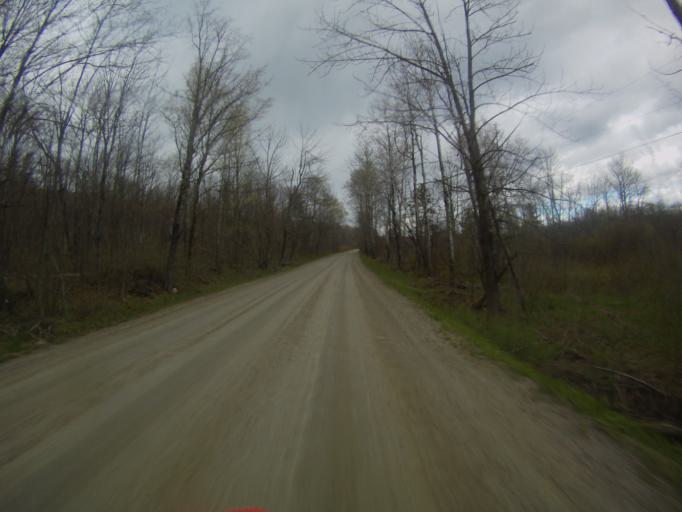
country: US
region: Vermont
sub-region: Addison County
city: Bristol
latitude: 44.0597
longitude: -73.0297
